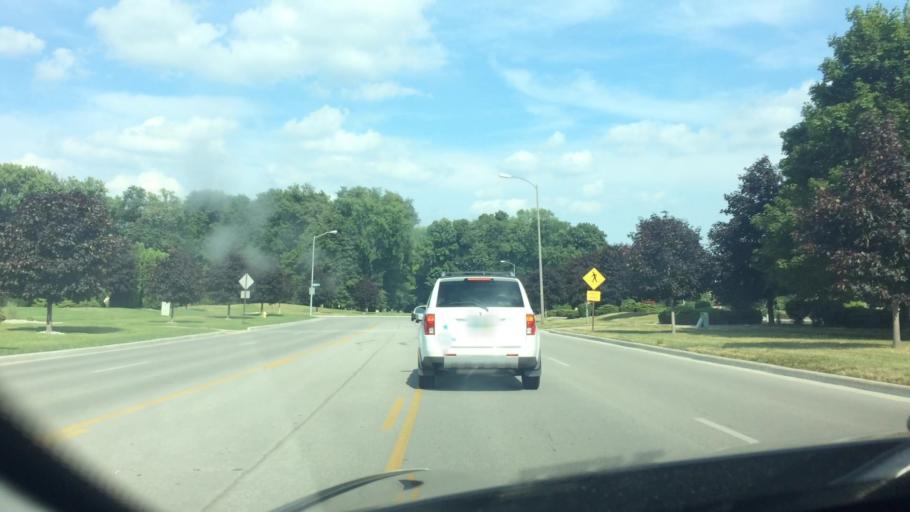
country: US
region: Ohio
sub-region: Lucas County
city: Maumee
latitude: 41.5854
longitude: -83.6624
